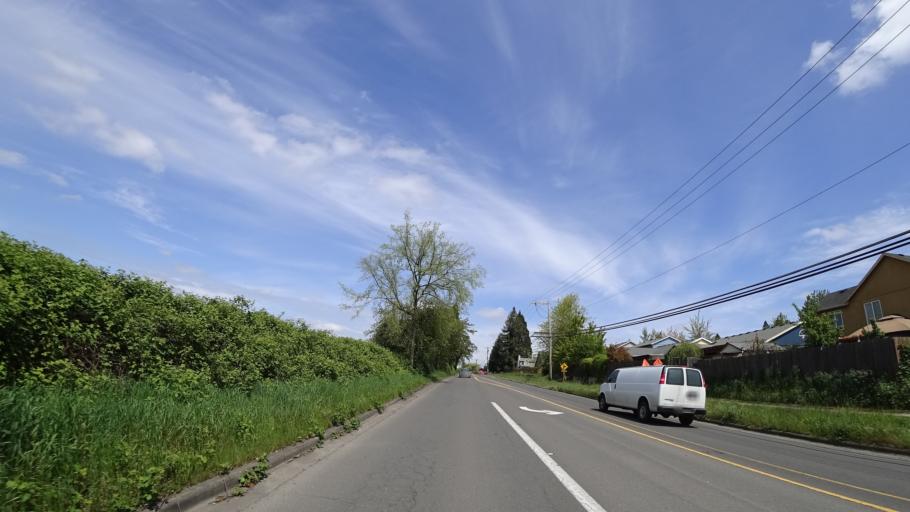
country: US
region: Oregon
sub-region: Washington County
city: Aloha
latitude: 45.4876
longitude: -122.8923
